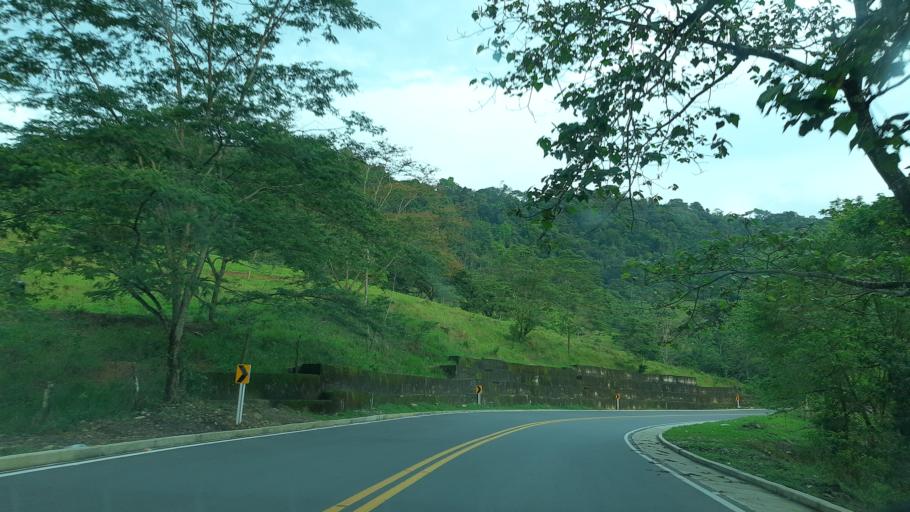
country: CO
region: Casanare
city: Sabanalarga
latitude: 4.7697
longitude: -73.0307
